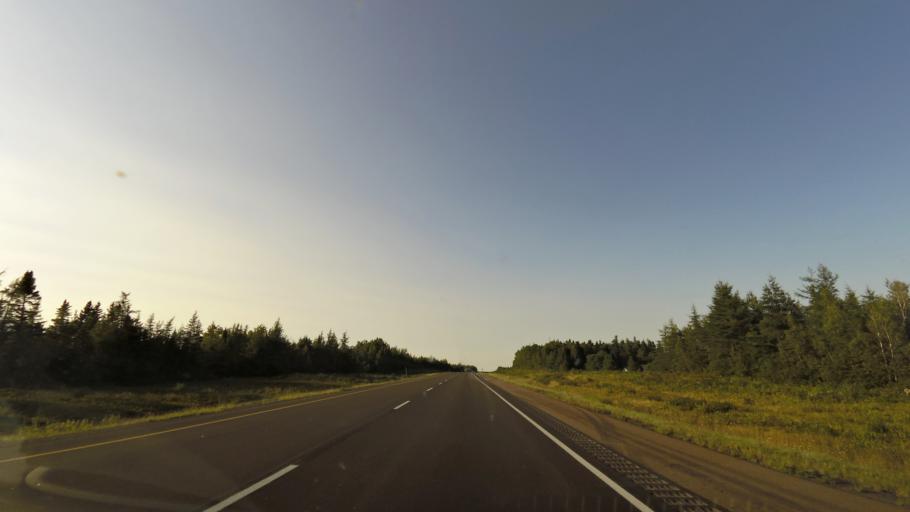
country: CA
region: New Brunswick
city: Dieppe
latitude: 46.0743
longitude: -64.5915
